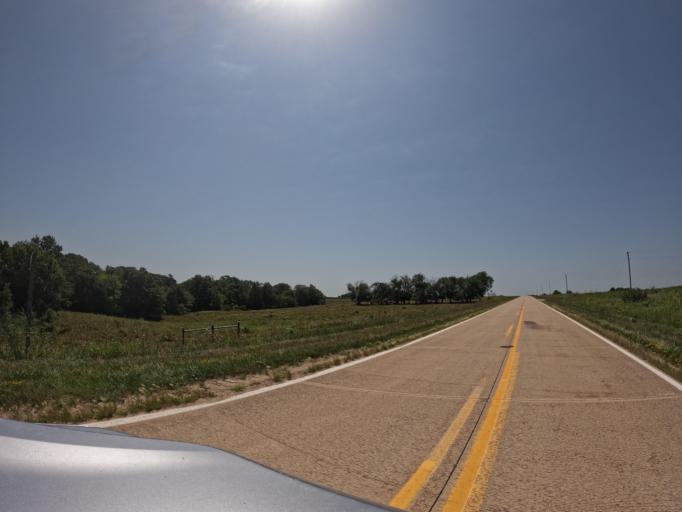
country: US
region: Iowa
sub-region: Henry County
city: Mount Pleasant
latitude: 40.8726
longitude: -91.5597
